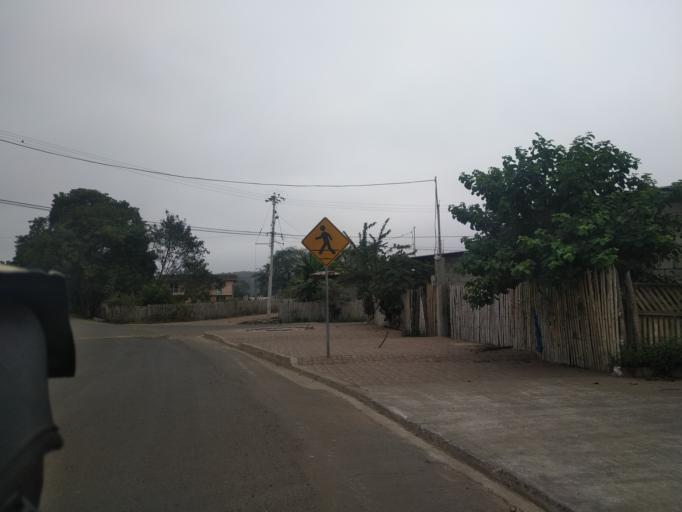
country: EC
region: Manabi
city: Montecristi
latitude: -1.0838
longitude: -80.6816
